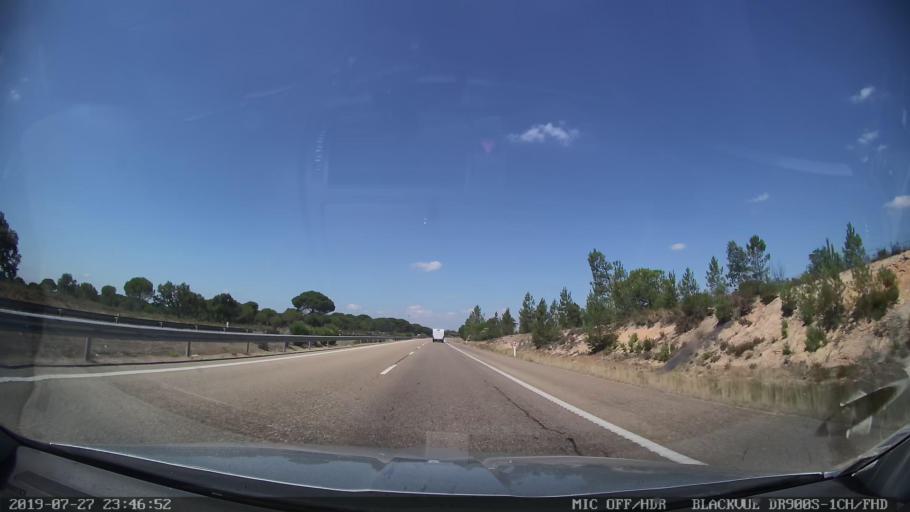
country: PT
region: Evora
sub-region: Vendas Novas
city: Vendas Novas
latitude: 38.6339
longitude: -8.5130
